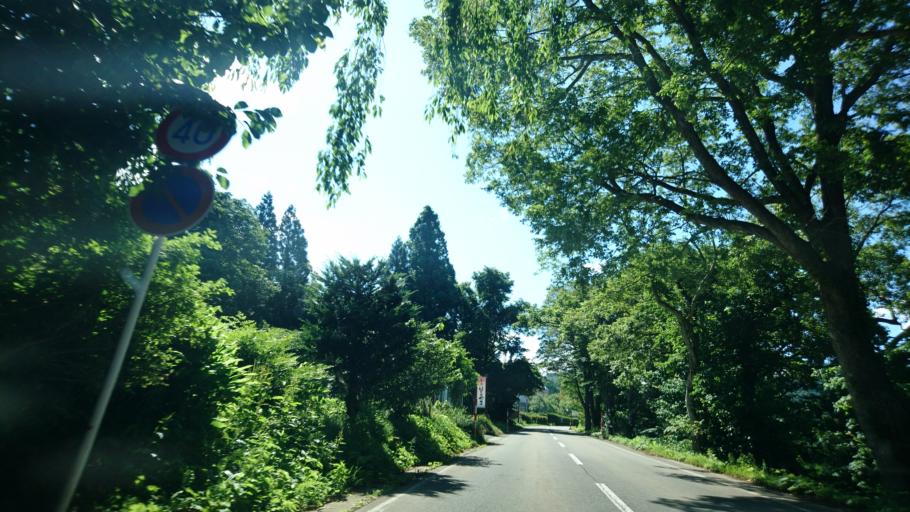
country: JP
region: Akita
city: Kakunodatemachi
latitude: 39.7390
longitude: 140.6925
